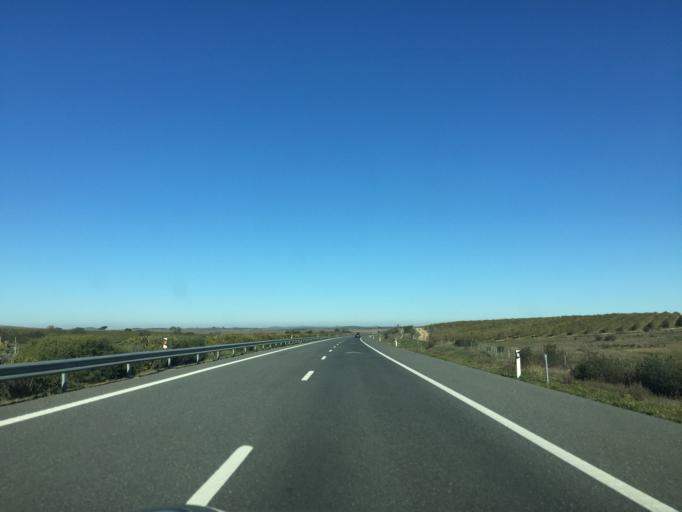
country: PT
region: Beja
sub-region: Ourique
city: Ourique
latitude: 37.7154
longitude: -8.1926
